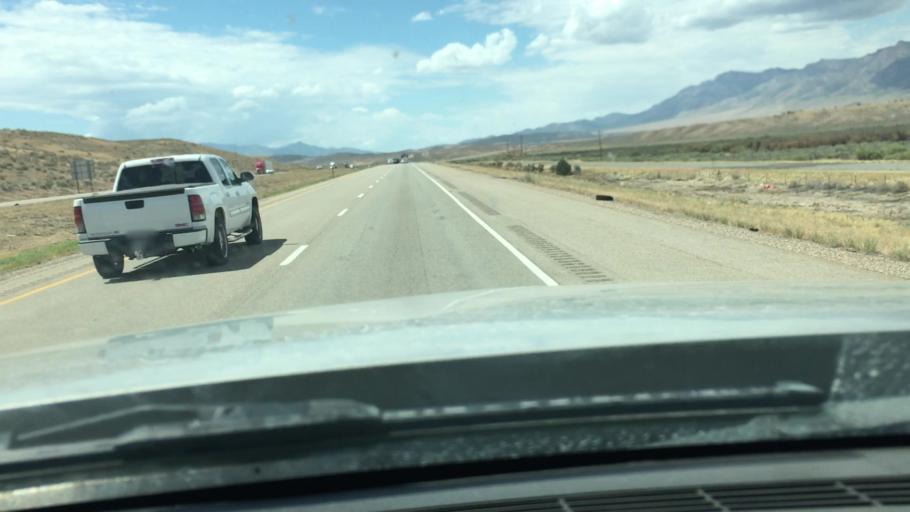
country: US
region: Utah
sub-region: Sanpete County
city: Gunnison
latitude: 39.4213
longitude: -112.0441
